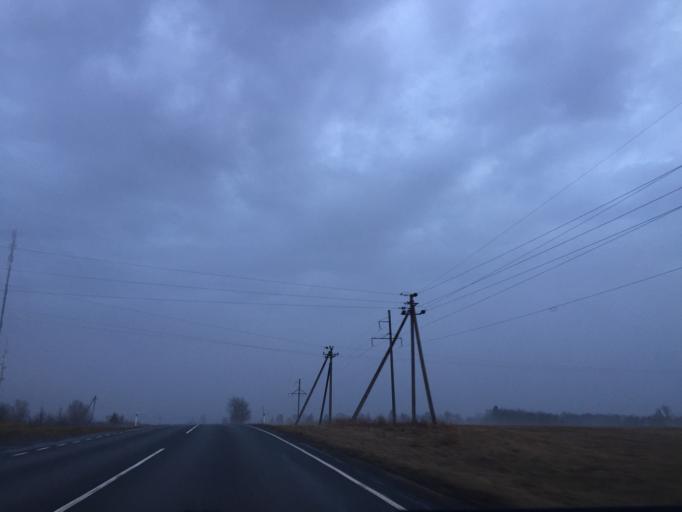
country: EE
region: Laeaene
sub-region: Lihula vald
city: Lihula
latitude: 58.6781
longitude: 23.8155
